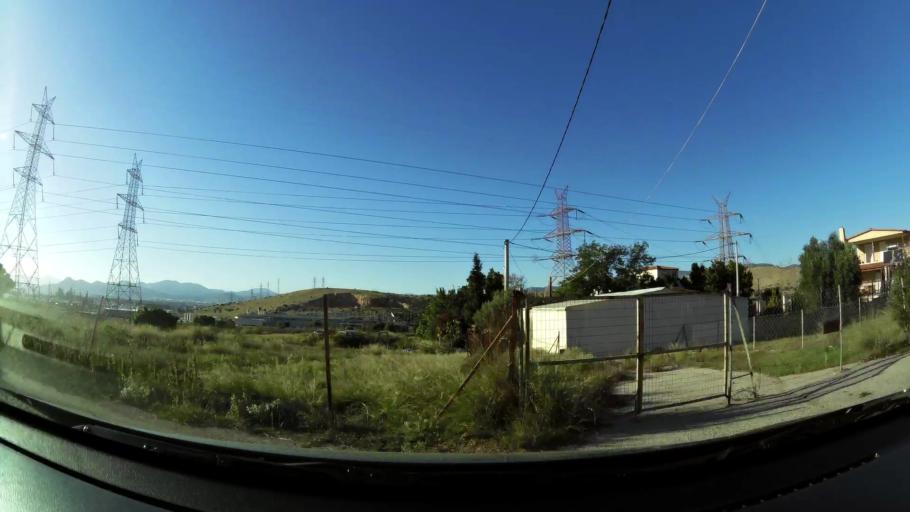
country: GR
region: Attica
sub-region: Nomarchia Athinas
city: Skaramangas
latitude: 38.0351
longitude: 23.6282
